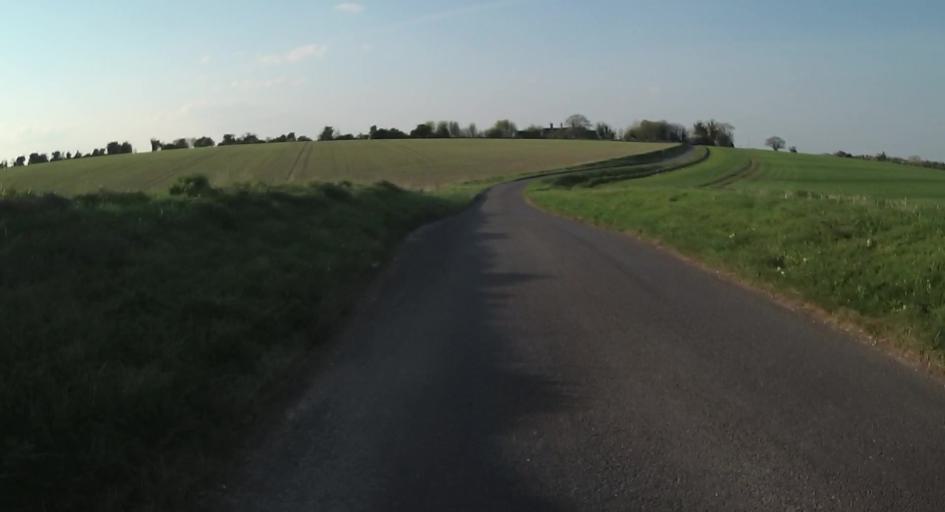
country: GB
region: England
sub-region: Hampshire
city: Basingstoke
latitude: 51.2279
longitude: -1.0917
